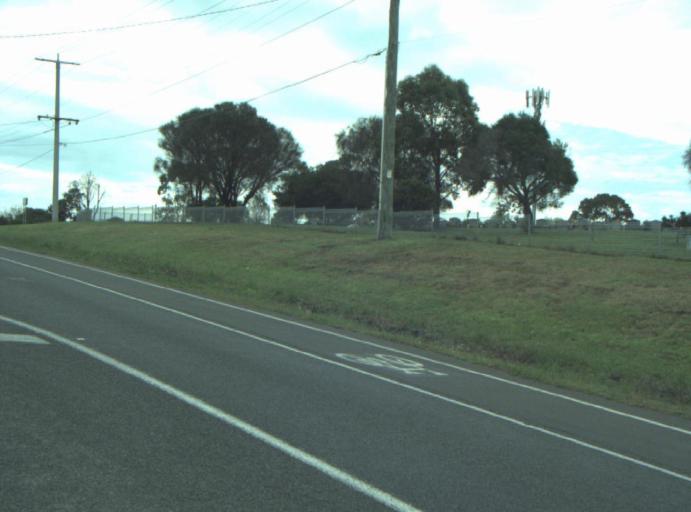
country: AU
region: Victoria
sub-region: Greater Geelong
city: East Geelong
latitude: -38.1661
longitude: 144.3850
